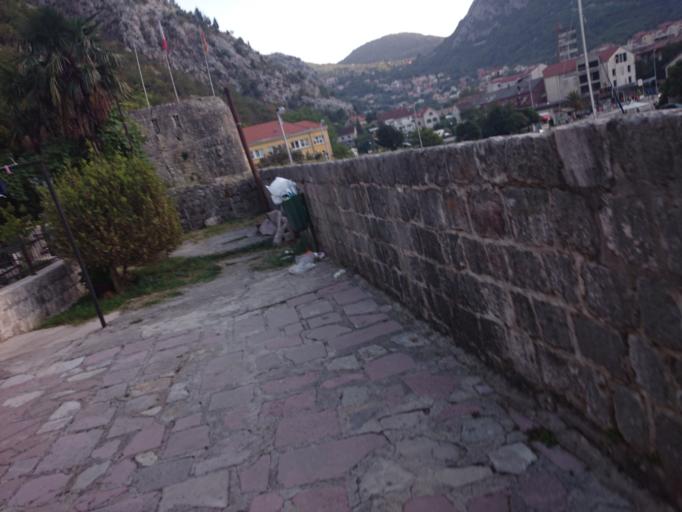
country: ME
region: Kotor
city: Kotor
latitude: 42.4227
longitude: 18.7715
